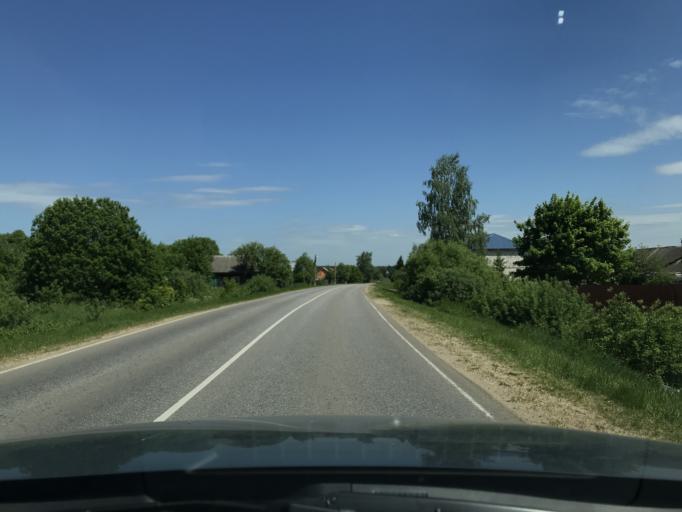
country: RU
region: Moskovskaya
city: Vereya
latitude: 55.3264
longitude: 36.2789
